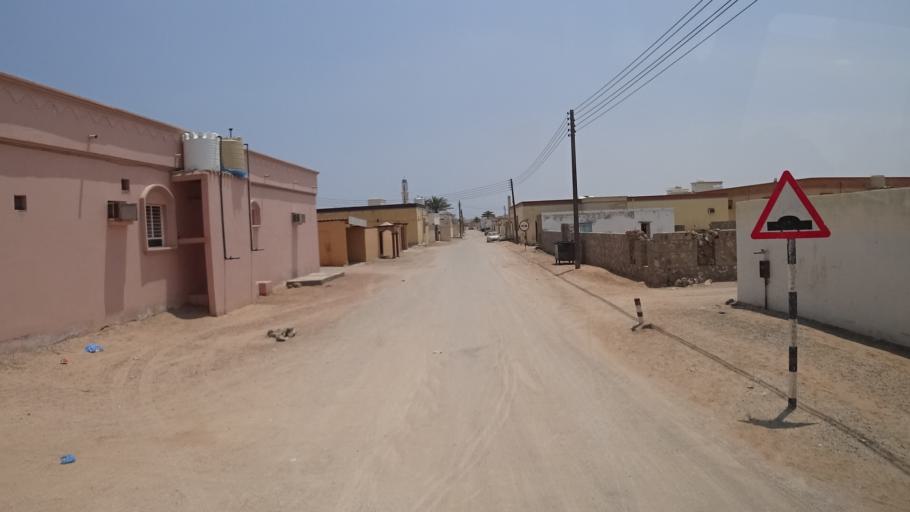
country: OM
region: Ash Sharqiyah
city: Sur
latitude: 22.5145
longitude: 59.7994
